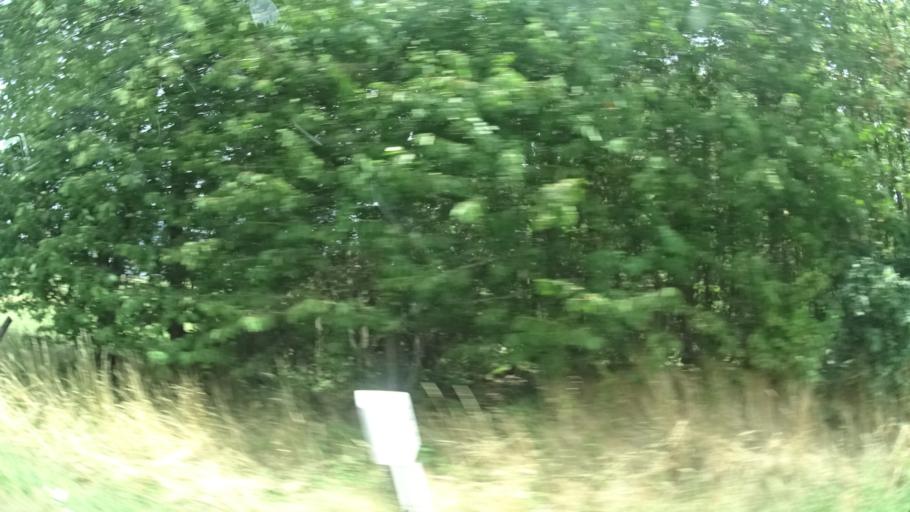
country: DE
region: Hesse
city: Gedern
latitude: 50.4044
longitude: 9.1960
